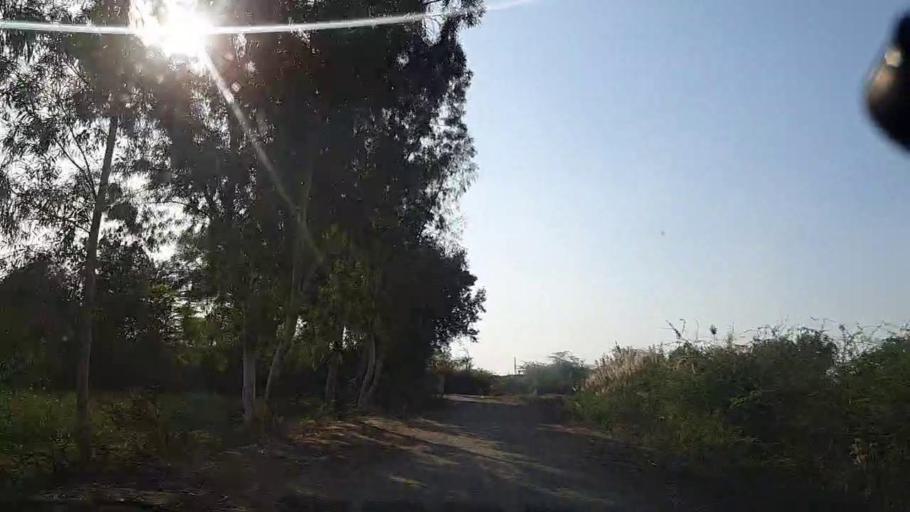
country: PK
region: Sindh
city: Mirpur Khas
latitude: 25.5619
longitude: 68.9669
